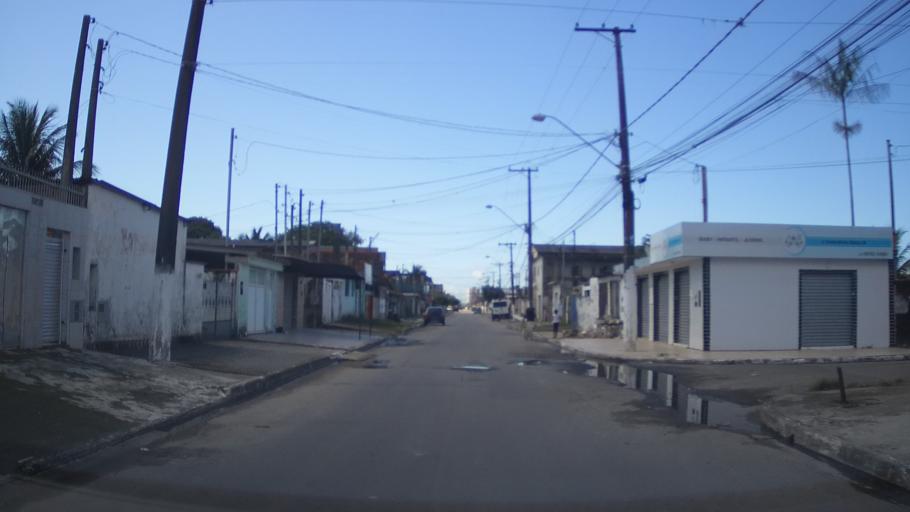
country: BR
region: Sao Paulo
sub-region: Mongagua
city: Mongagua
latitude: -24.0341
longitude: -46.5343
